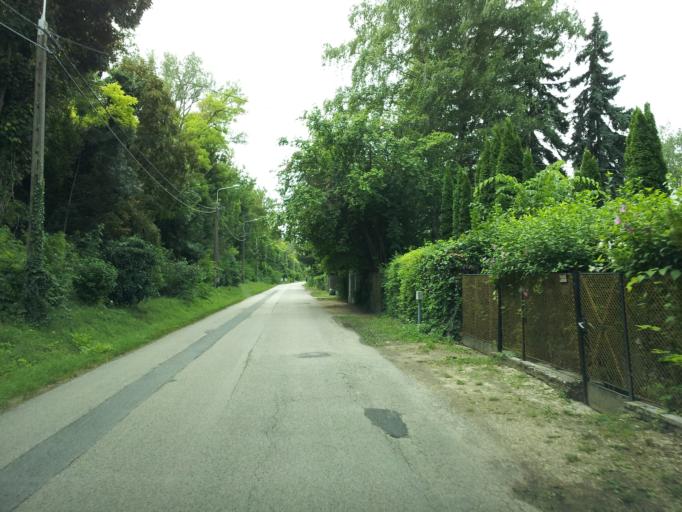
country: HU
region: Somogy
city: Balatonszabadi
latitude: 46.9701
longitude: 18.1606
